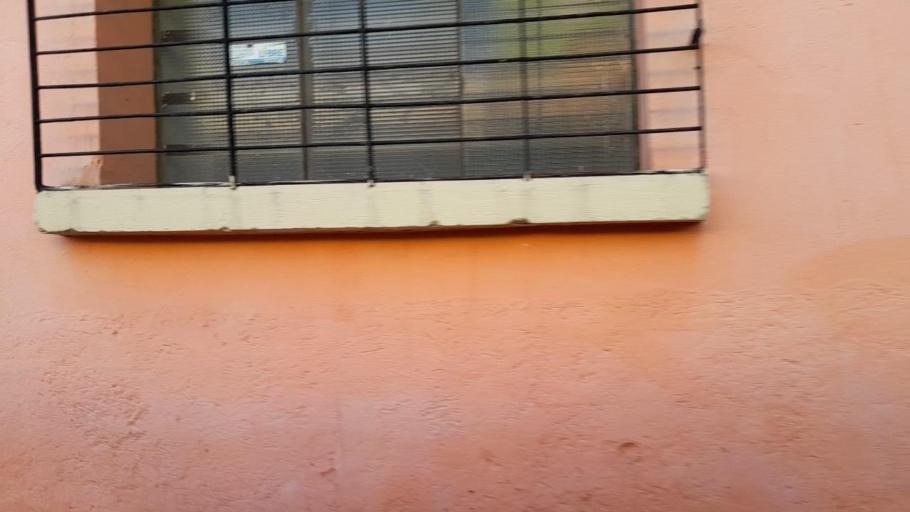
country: GT
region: Quetzaltenango
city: Quetzaltenango
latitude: 14.8395
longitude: -91.5145
